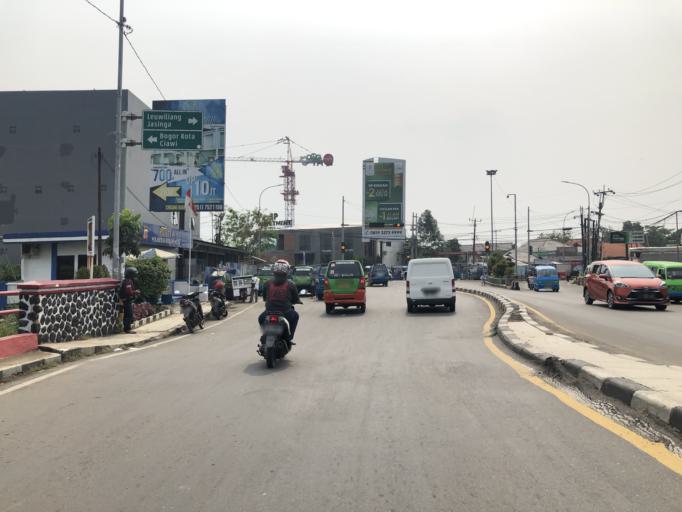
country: ID
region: West Java
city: Bogor
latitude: -6.5732
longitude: 106.7520
